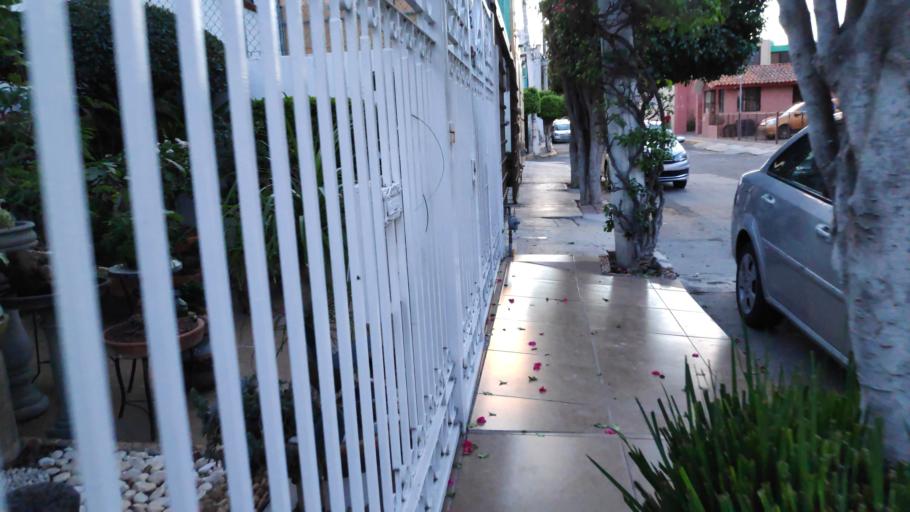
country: MX
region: Queretaro
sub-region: Queretaro
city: Santiago de Queretaro
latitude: 20.5826
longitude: -100.3822
